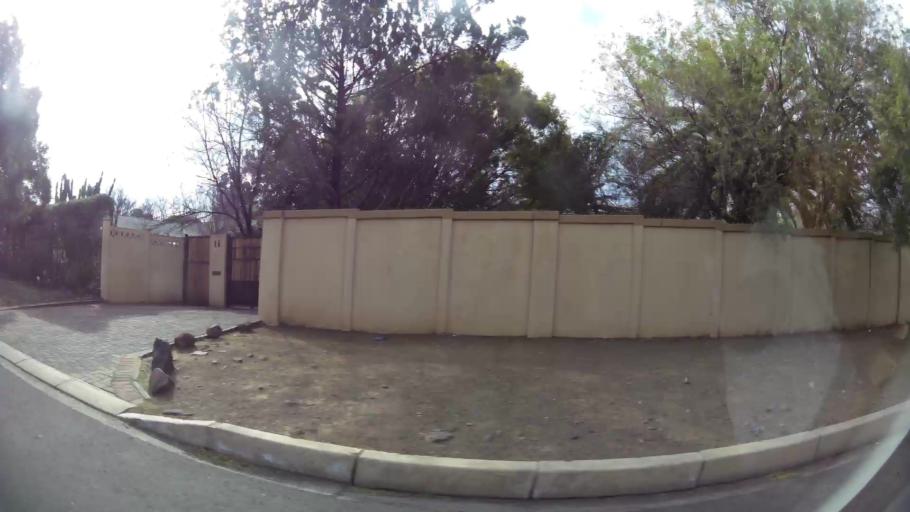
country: ZA
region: Orange Free State
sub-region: Mangaung Metropolitan Municipality
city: Bloemfontein
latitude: -29.0914
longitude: 26.2497
